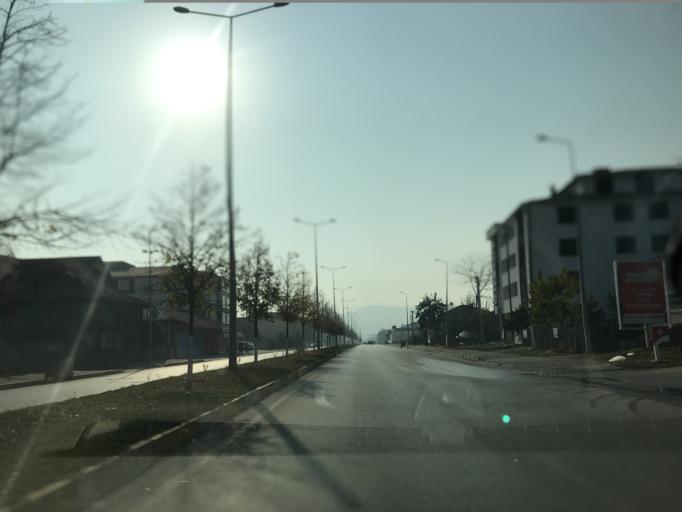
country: TR
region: Duzce
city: Cumayeri
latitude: 40.8681
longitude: 30.9520
